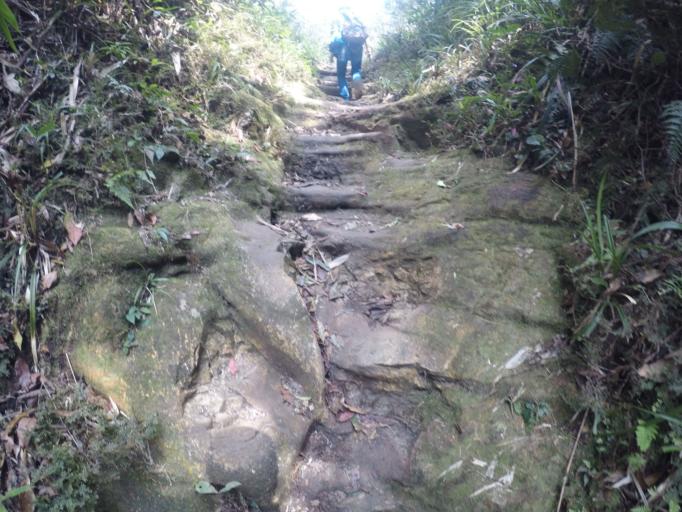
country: VN
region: Lao Cai
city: Sa Pa
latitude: 22.3507
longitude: 103.7746
